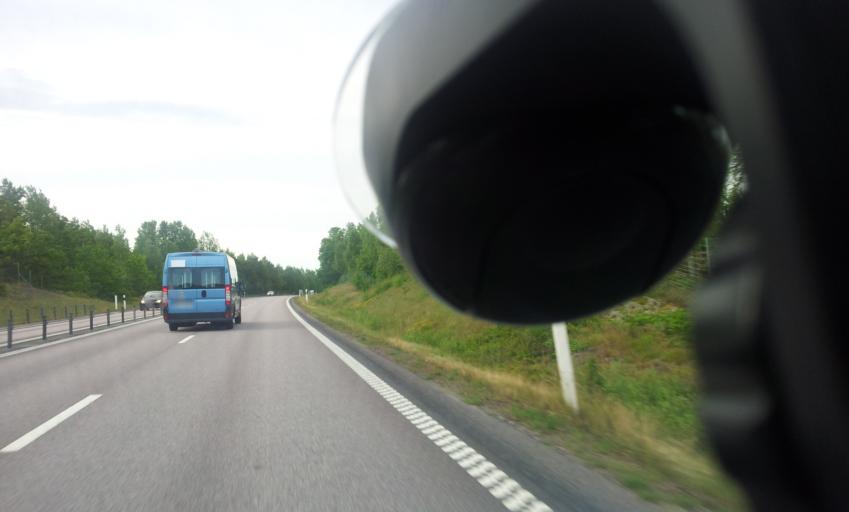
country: SE
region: Kalmar
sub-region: Oskarshamns Kommun
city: Paskallavik
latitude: 57.2073
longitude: 16.4367
